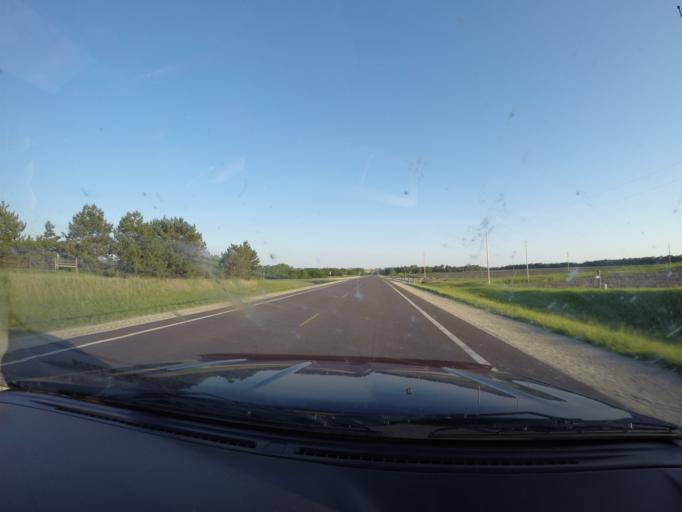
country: US
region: Kansas
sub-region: Marshall County
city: Blue Rapids
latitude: 39.6543
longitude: -96.7506
